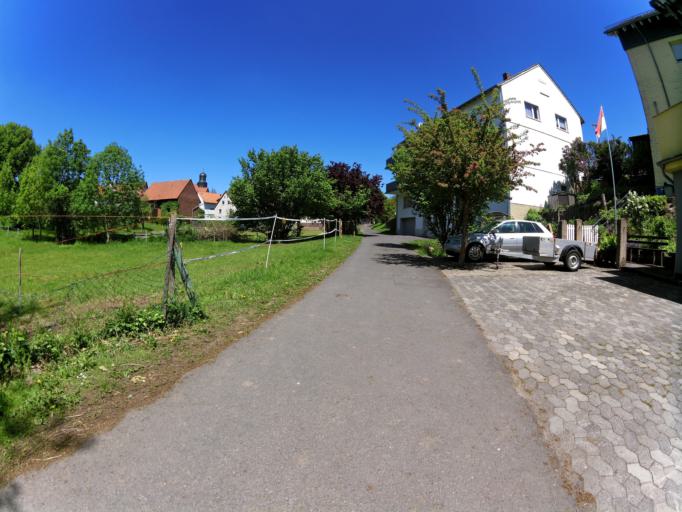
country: DE
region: Thuringia
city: Dankmarshausen
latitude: 50.9502
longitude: 9.9930
